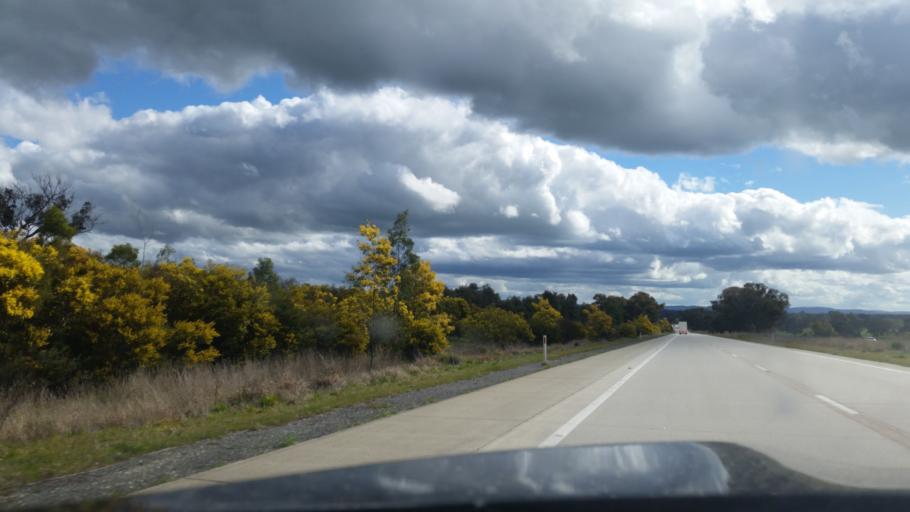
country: AU
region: New South Wales
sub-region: Greater Hume Shire
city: Jindera
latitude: -35.9245
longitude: 147.0491
